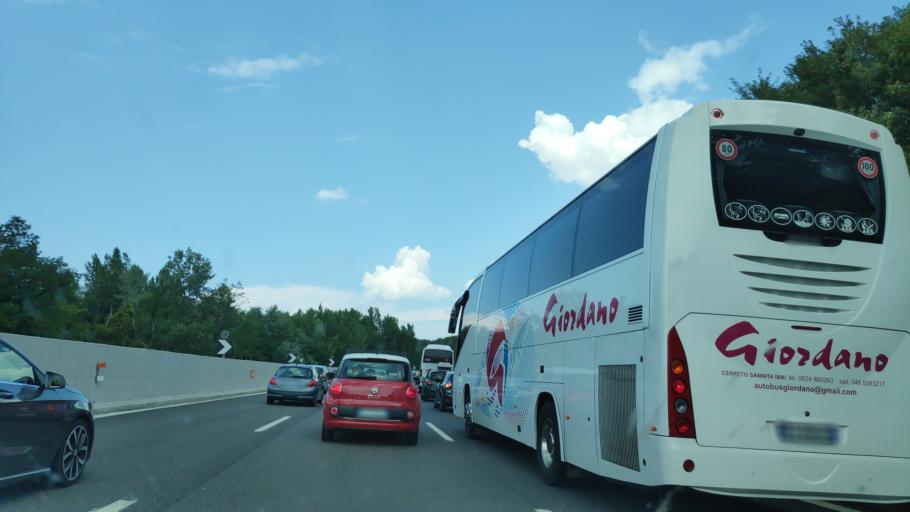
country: IT
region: Umbria
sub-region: Provincia di Terni
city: Stazione di Allerona
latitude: 42.8156
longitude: 12.0321
